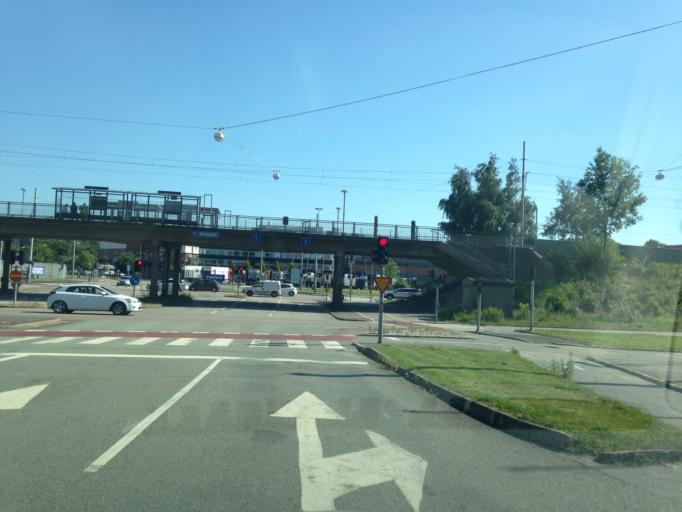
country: SE
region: Vaestra Goetaland
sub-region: Goteborg
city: Majorna
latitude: 57.7188
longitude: 11.9187
